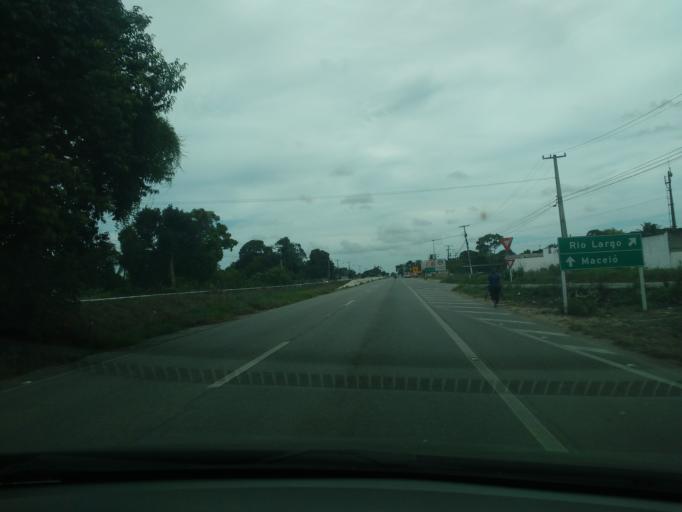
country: BR
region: Alagoas
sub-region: Rio Largo
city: Rio Largo
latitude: -9.4727
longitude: -35.8227
